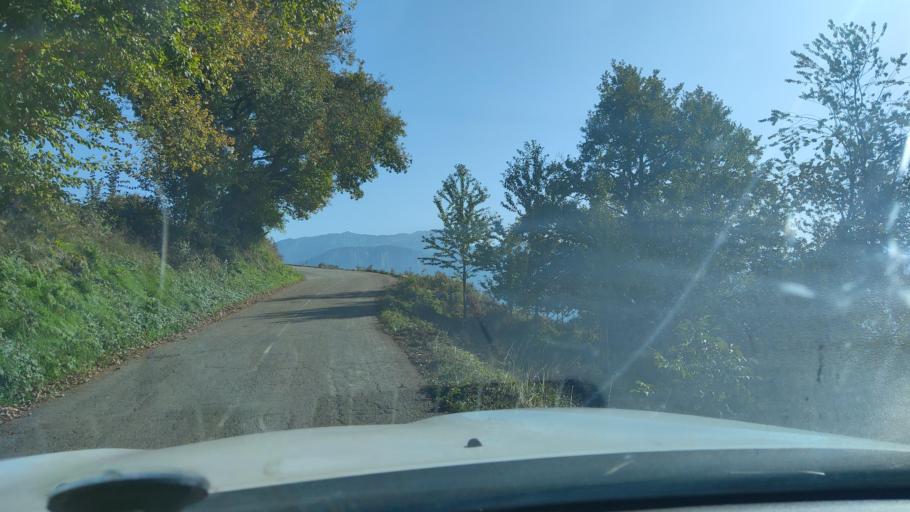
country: FR
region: Rhone-Alpes
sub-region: Departement de la Savoie
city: Les Echelles
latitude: 45.4637
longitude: 5.7652
